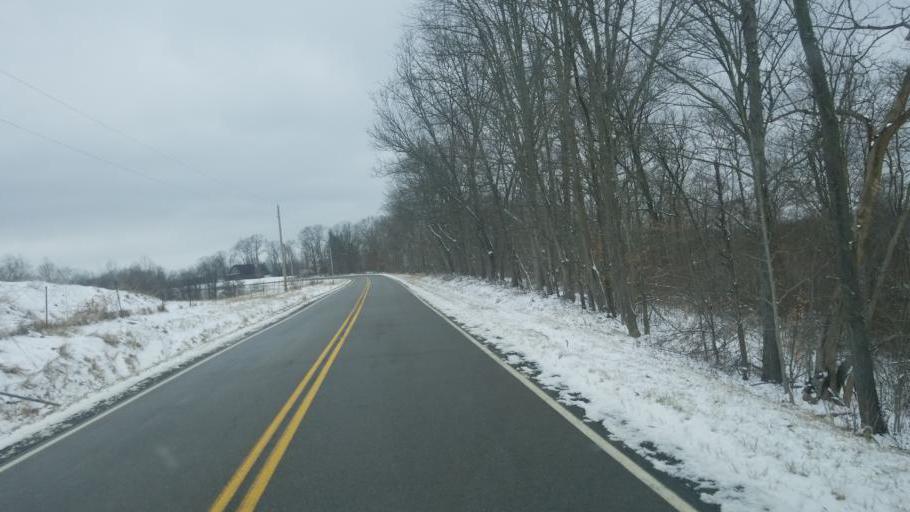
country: US
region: Ohio
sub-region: Knox County
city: Oak Hill
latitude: 40.3768
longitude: -82.1406
